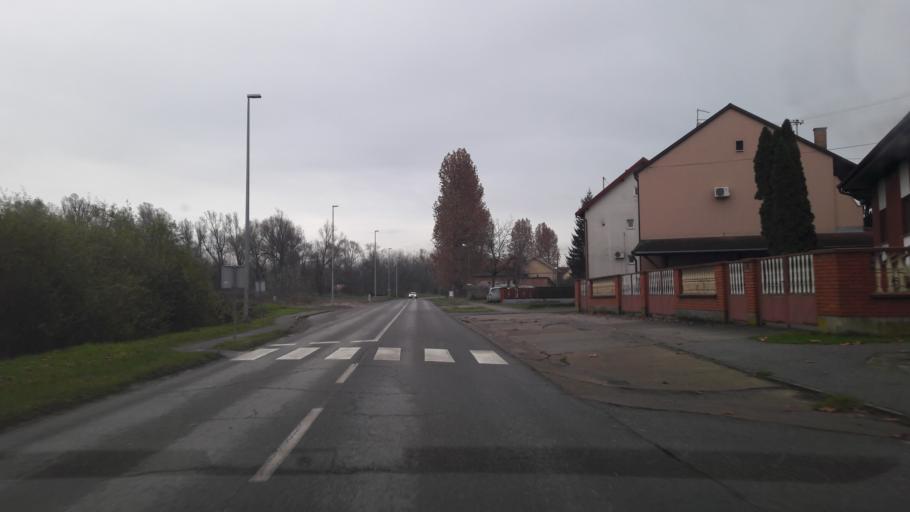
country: HR
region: Osjecko-Baranjska
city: Visnjevac
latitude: 45.5737
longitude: 18.5982
